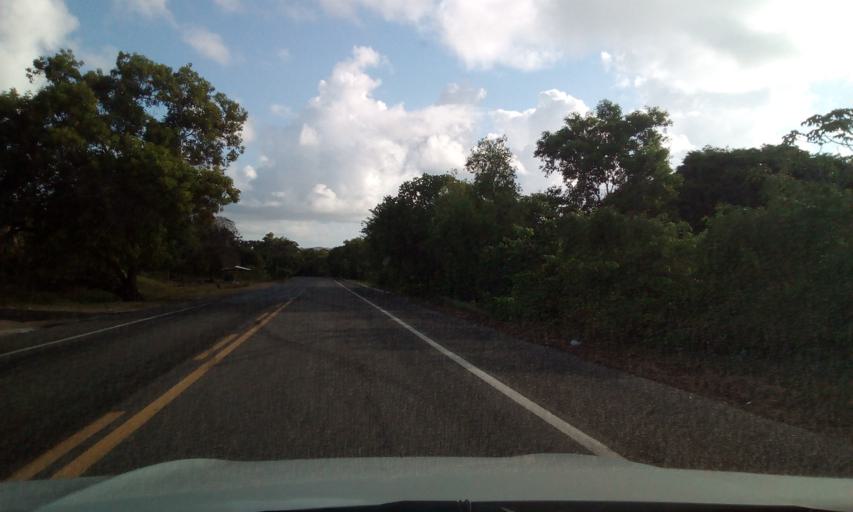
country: BR
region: Bahia
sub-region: Mata De Sao Joao
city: Mata de Sao Joao
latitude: -12.3966
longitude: -37.9180
